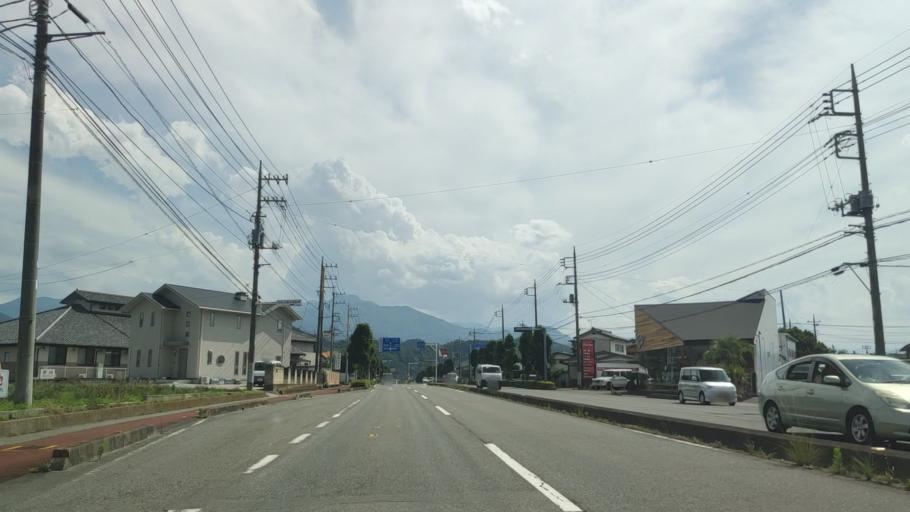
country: JP
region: Gunma
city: Tomioka
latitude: 36.2522
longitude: 138.8617
